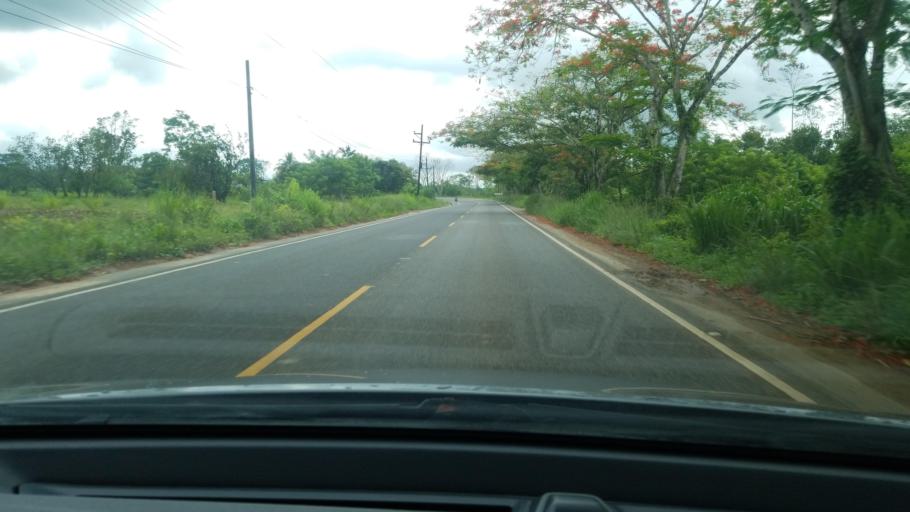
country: HN
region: Cortes
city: Potrerillos
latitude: 15.5958
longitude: -88.3164
